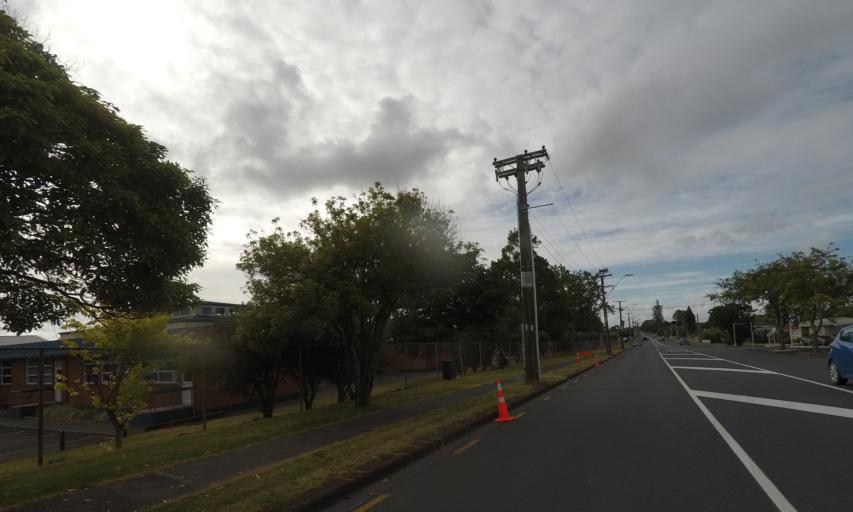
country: NZ
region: Northland
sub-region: Whangarei
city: Whangarei
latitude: -35.6849
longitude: 174.3018
